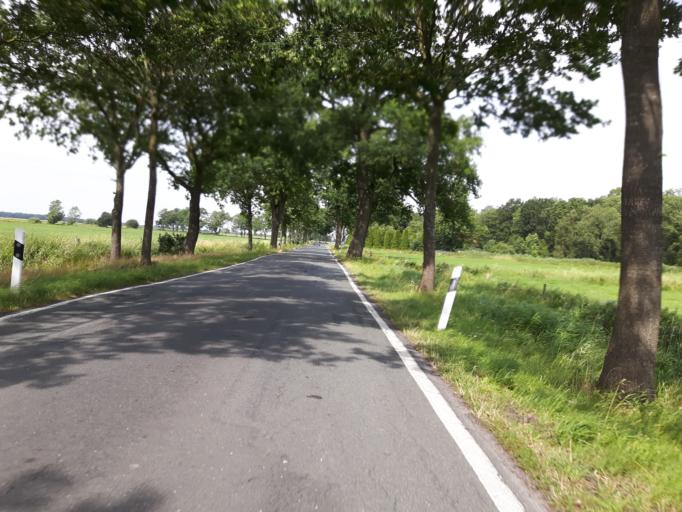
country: DE
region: Lower Saxony
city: Rastede
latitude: 53.3296
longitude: 8.2622
